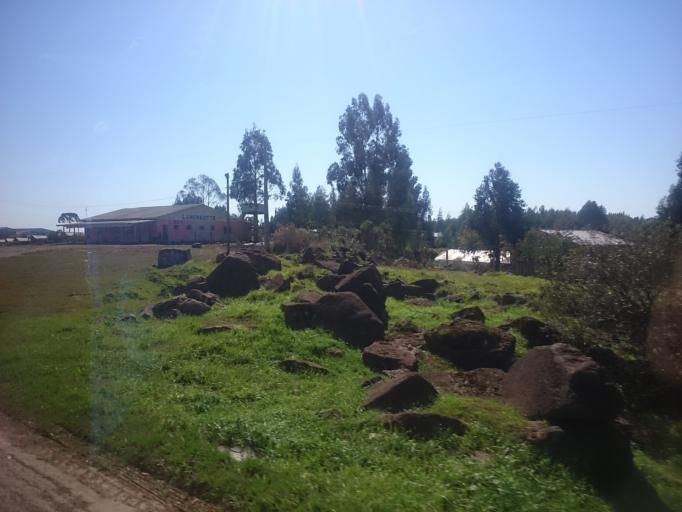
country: BR
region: Santa Catarina
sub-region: Santa Cecilia
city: Santa Cecilia
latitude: -26.9809
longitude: -50.3946
